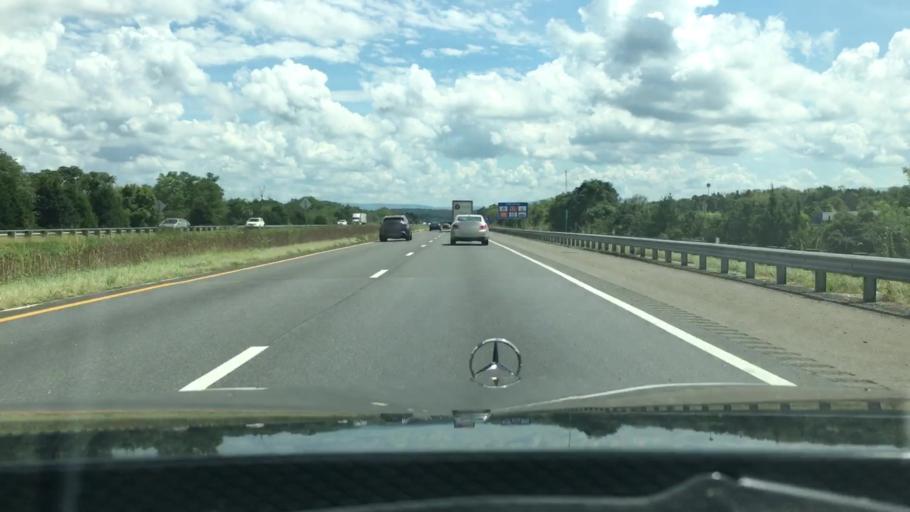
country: US
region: Virginia
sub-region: Shenandoah County
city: Strasburg
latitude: 39.0132
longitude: -78.3478
